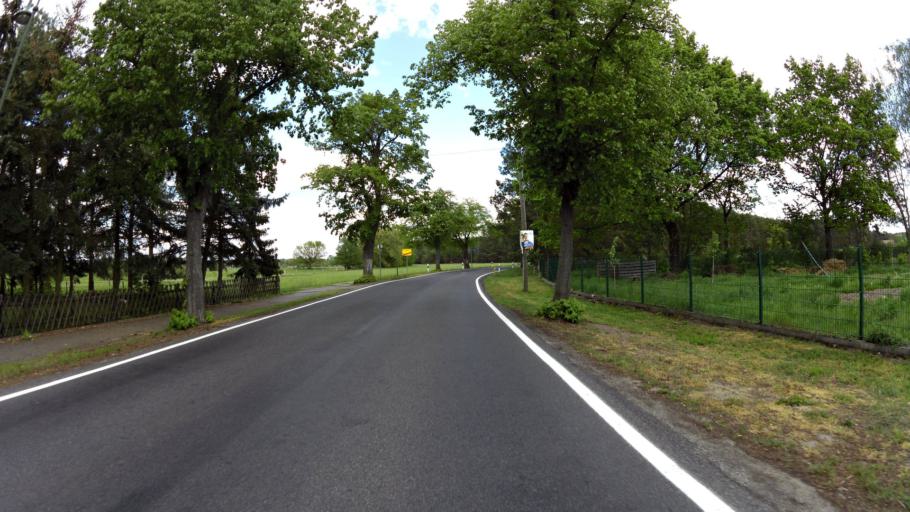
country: DE
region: Brandenburg
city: Schlepzig
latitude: 52.0971
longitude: 13.9062
